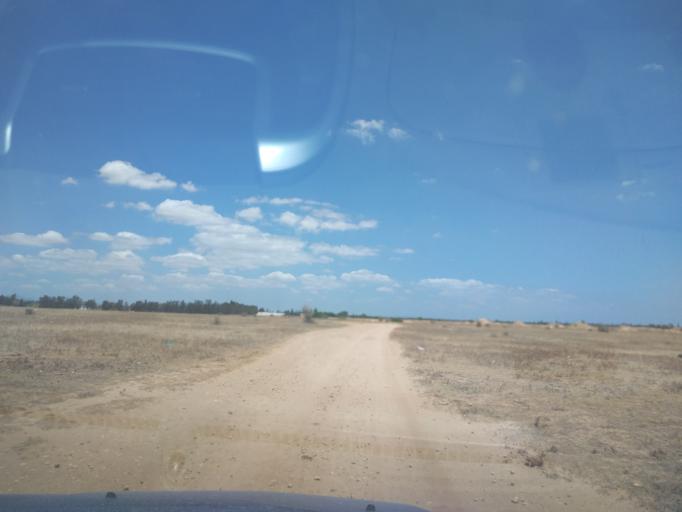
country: TN
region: Susah
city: Harqalah
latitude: 36.1716
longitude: 10.4355
